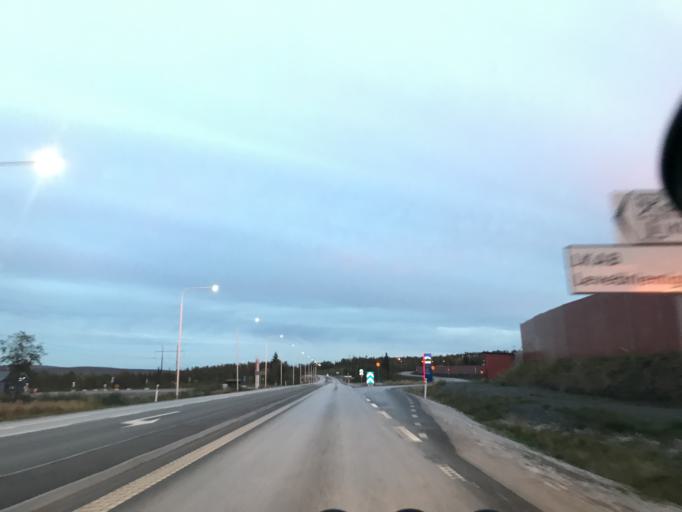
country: SE
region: Norrbotten
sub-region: Gallivare Kommun
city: Malmberget
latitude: 67.6538
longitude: 21.0143
